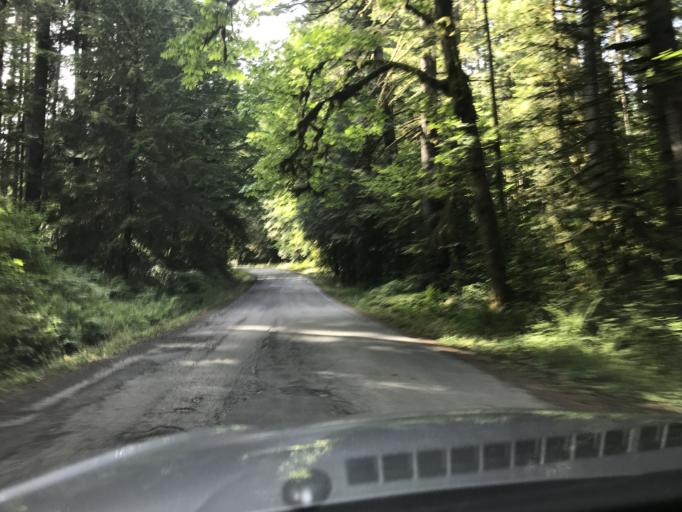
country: US
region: Washington
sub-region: King County
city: Hobart
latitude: 47.4152
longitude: -121.9280
